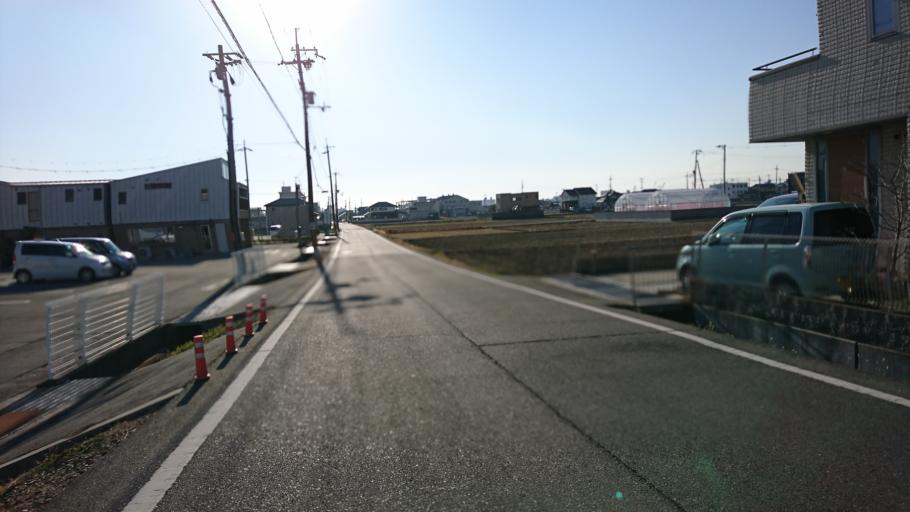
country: JP
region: Hyogo
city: Kakogawacho-honmachi
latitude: 34.7732
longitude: 134.8595
